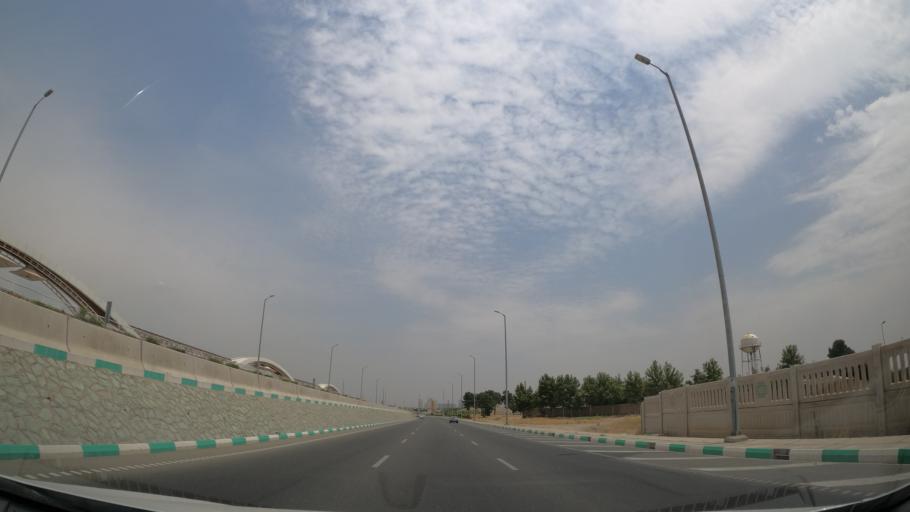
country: IR
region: Tehran
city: Shahr-e Qods
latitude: 35.7393
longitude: 51.2159
